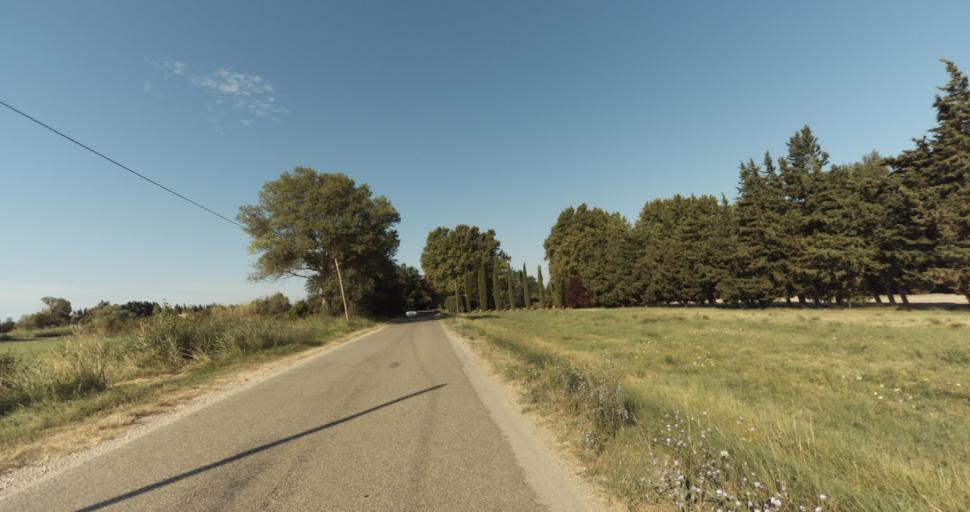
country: FR
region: Provence-Alpes-Cote d'Azur
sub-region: Departement du Vaucluse
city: Sarrians
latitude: 44.0541
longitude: 4.9646
